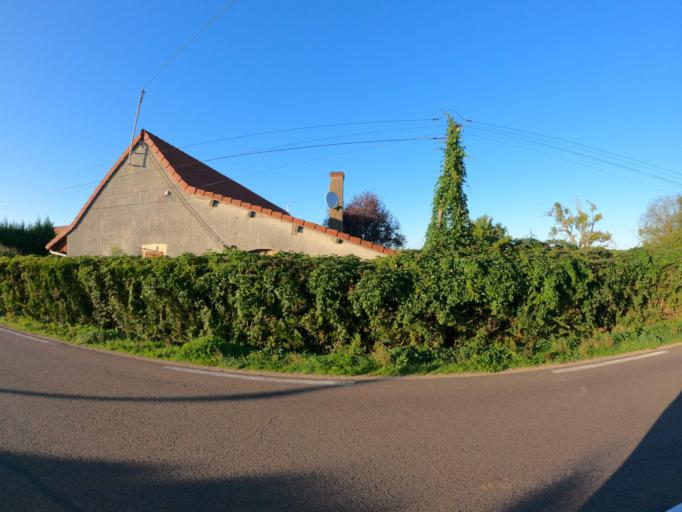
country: FR
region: Bourgogne
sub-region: Departement de Saone-et-Loire
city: Saint-Germain-du-Plain
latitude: 46.7532
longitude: 5.0237
